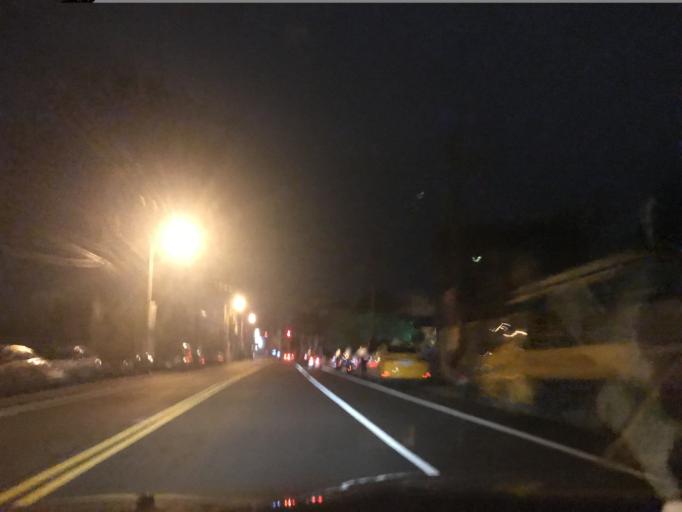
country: TW
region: Taiwan
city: Taoyuan City
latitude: 24.9420
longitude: 121.2431
